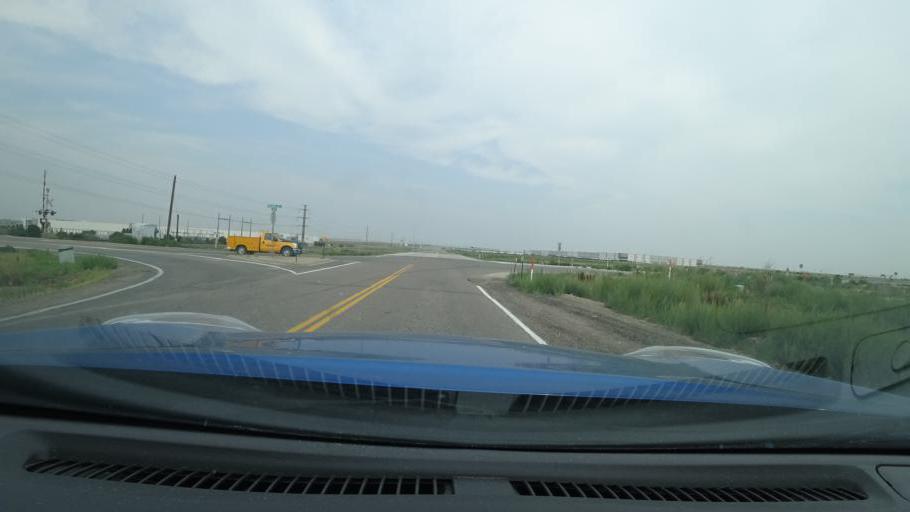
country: US
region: Colorado
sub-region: Adams County
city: Aurora
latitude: 39.7503
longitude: -104.7352
